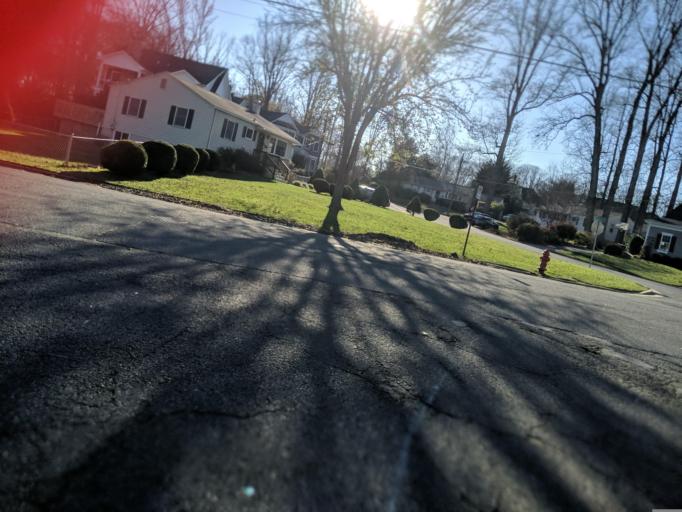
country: US
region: Virginia
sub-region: Fairfax County
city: Vienna
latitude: 38.8914
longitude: -77.2547
